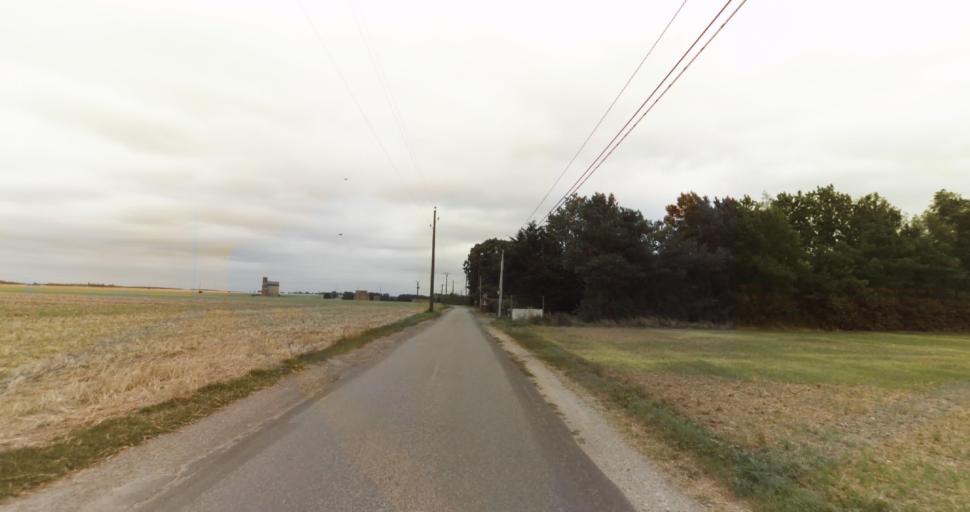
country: FR
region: Haute-Normandie
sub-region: Departement de l'Eure
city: La Couture-Boussey
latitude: 48.9308
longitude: 1.3345
